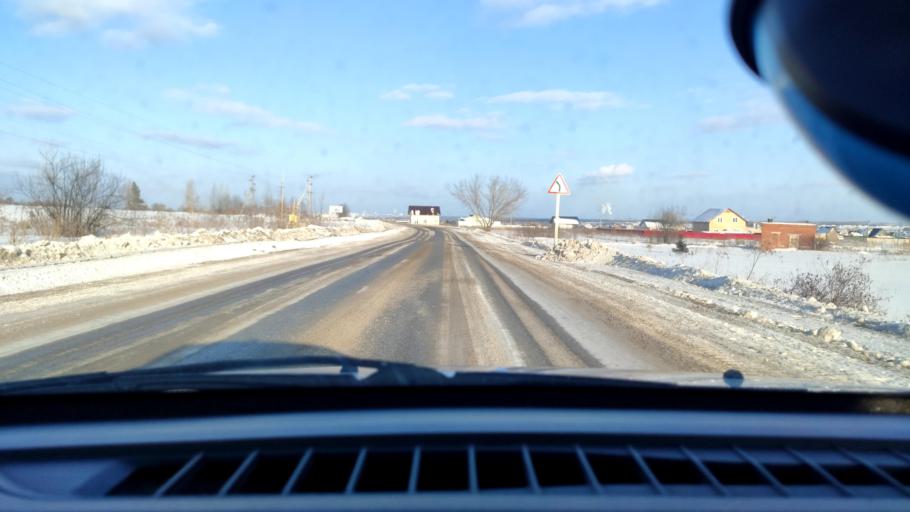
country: RU
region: Perm
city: Kultayevo
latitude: 57.9209
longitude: 55.9553
